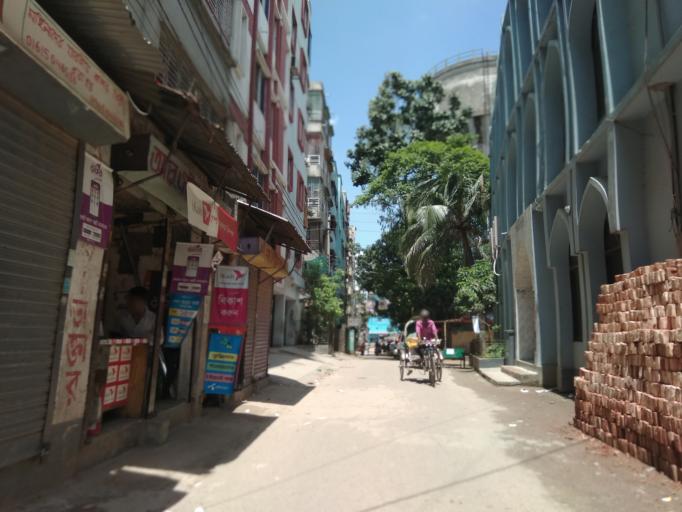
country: BD
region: Dhaka
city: Tungi
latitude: 23.8292
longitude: 90.3709
